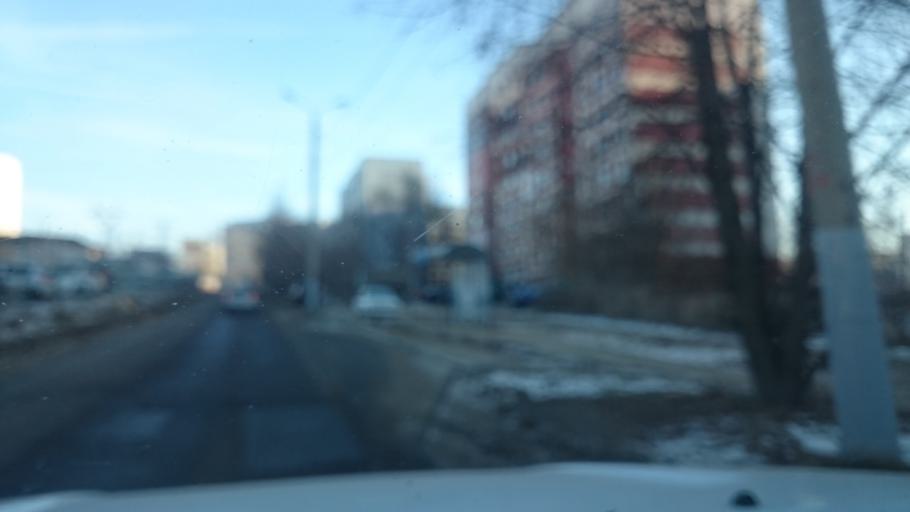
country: RU
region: Tula
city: Tula
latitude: 54.2126
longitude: 37.6863
